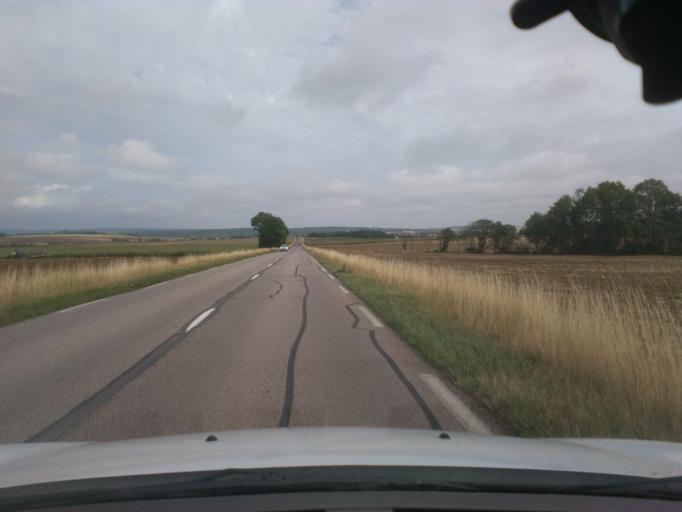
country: FR
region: Lorraine
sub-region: Departement de Meurthe-et-Moselle
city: Pulligny
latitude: 48.4953
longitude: 6.1472
